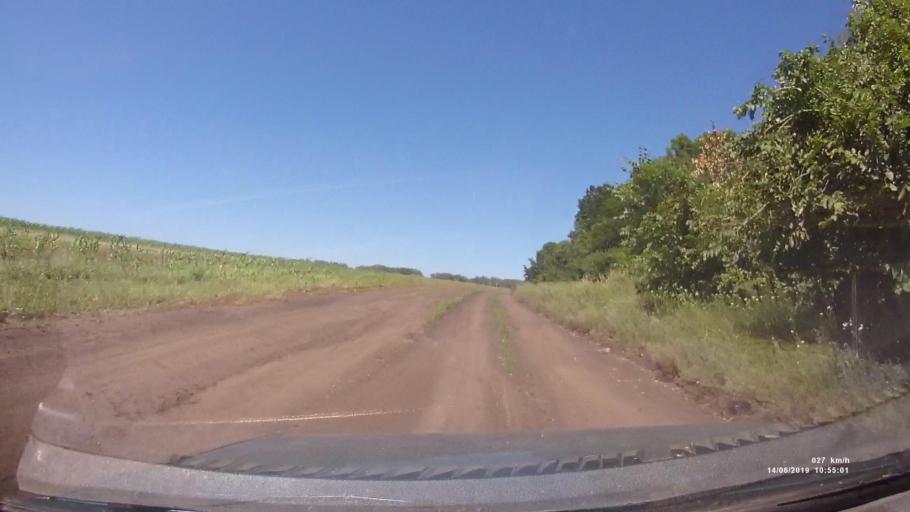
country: RU
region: Rostov
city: Kazanskaya
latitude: 49.8625
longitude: 41.3743
